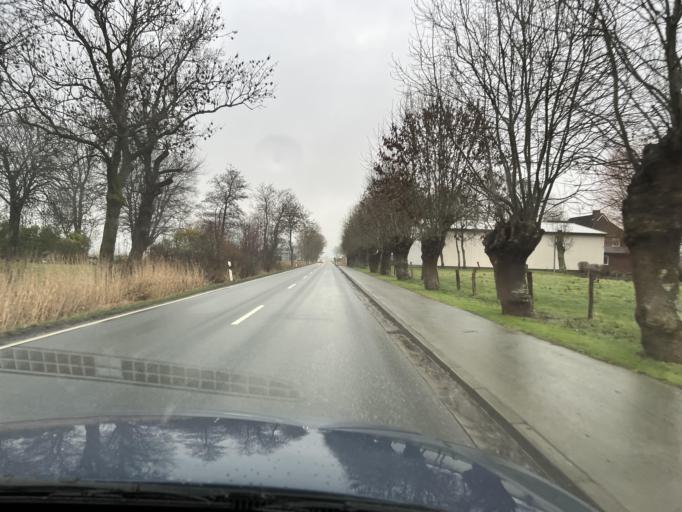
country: DE
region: Schleswig-Holstein
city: Oesterwurth
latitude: 54.2127
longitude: 8.9848
